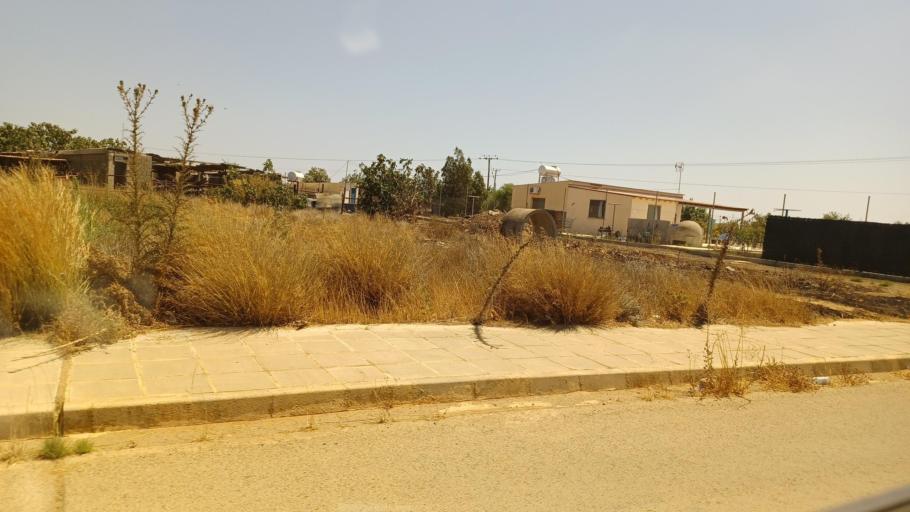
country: CY
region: Ammochostos
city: Acheritou
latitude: 35.0701
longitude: 33.8885
